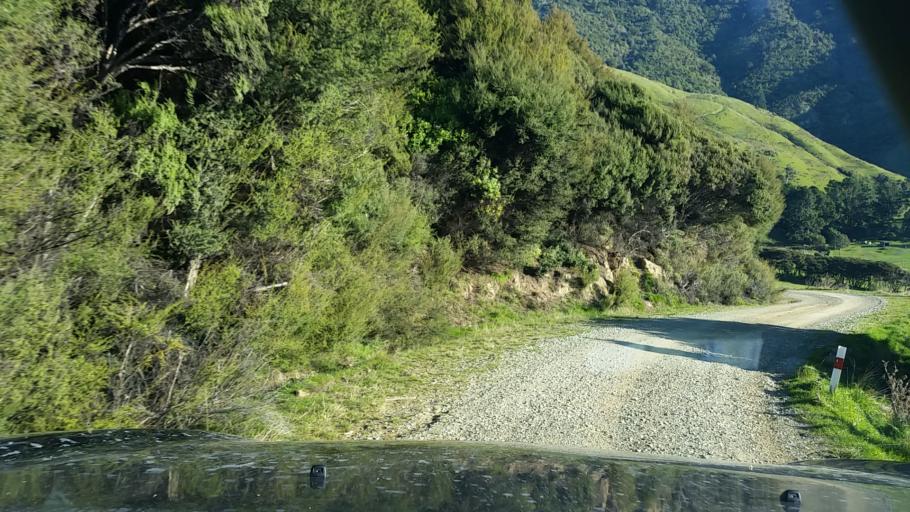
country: NZ
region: Marlborough
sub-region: Marlborough District
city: Picton
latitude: -41.0193
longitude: 174.1393
